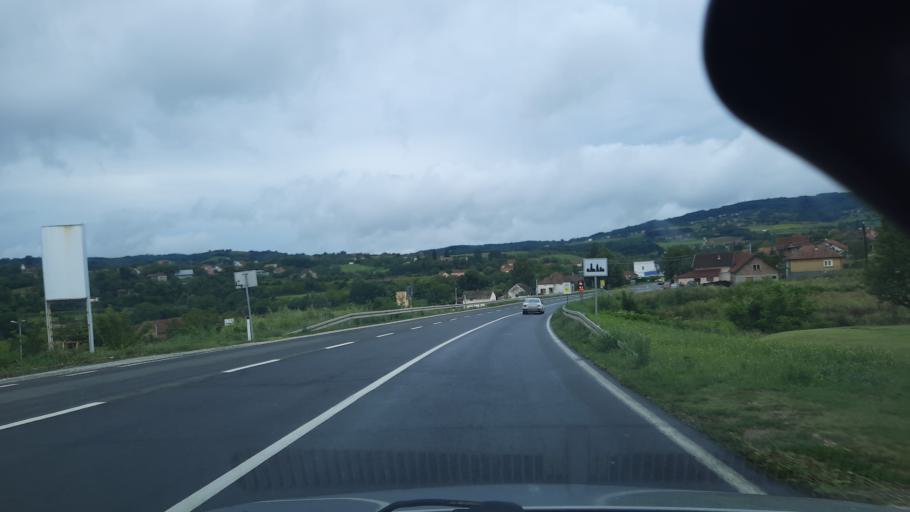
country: RS
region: Central Serbia
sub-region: Sumadijski Okrug
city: Kragujevac
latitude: 43.9775
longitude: 20.8272
